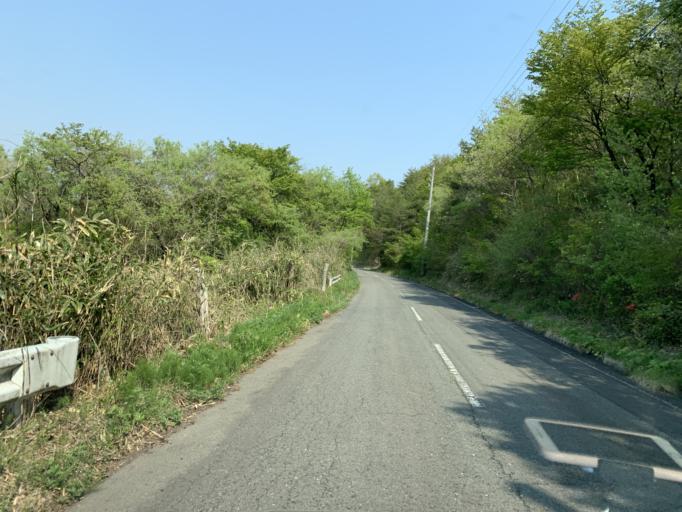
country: JP
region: Iwate
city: Ichinoseki
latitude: 38.8904
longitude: 141.0652
